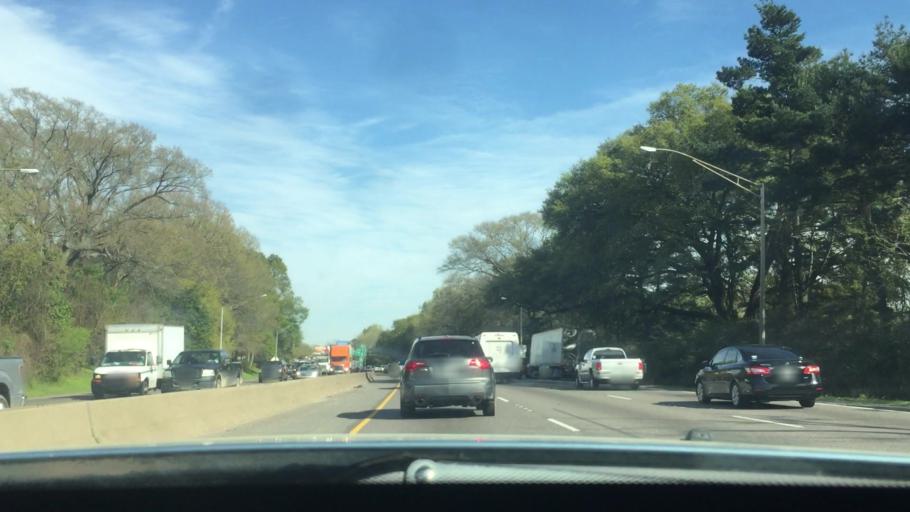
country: US
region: Louisiana
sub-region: East Baton Rouge Parish
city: Baton Rouge
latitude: 30.4260
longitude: -91.1658
